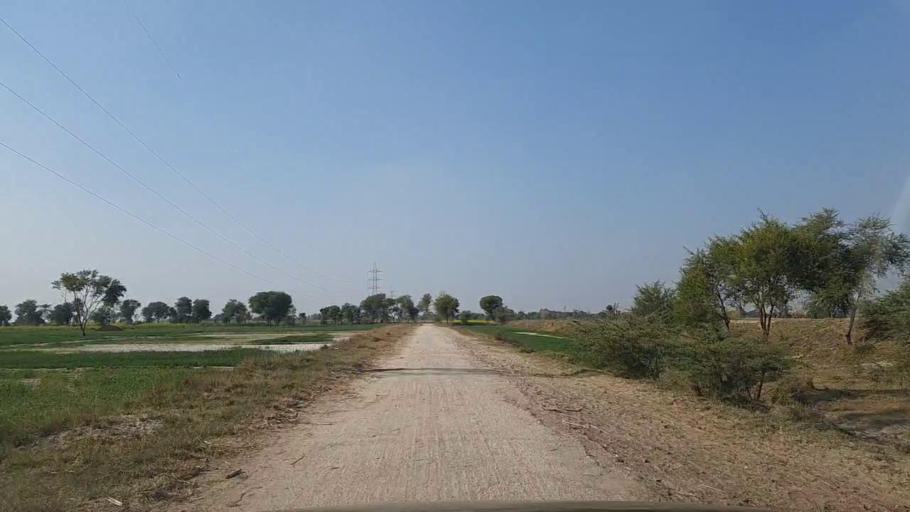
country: PK
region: Sindh
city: Daur
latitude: 26.3834
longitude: 68.3277
